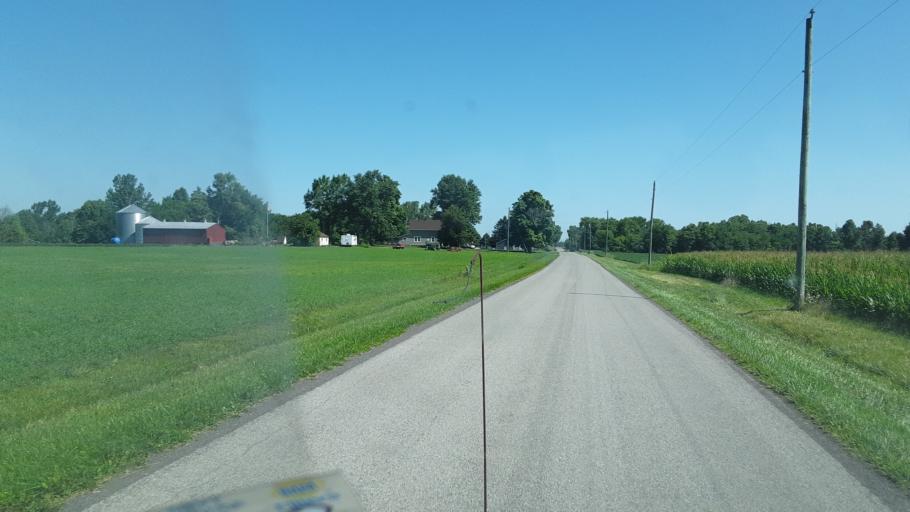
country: US
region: Ohio
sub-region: Union County
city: Richwood
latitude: 40.3415
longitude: -83.3358
